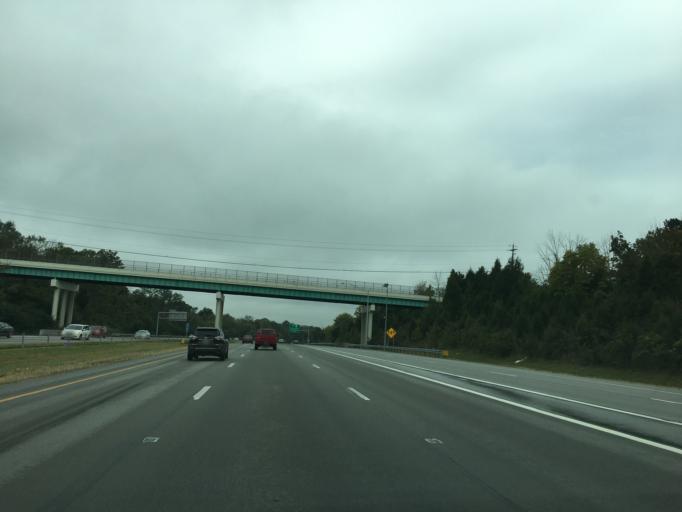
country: US
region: Ohio
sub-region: Hamilton County
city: Dry Ridge
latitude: 39.2282
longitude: -84.6417
